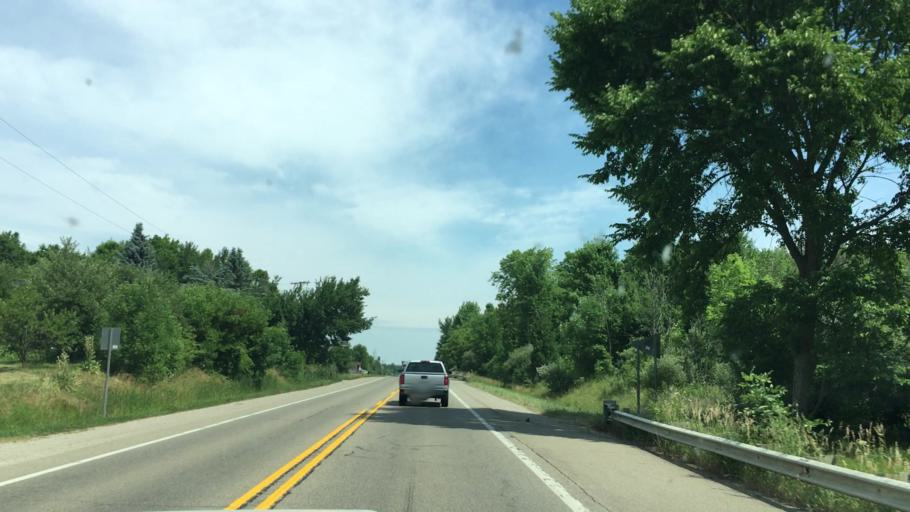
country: US
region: Michigan
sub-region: Lapeer County
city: Imlay City
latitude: 43.0752
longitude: -83.0753
